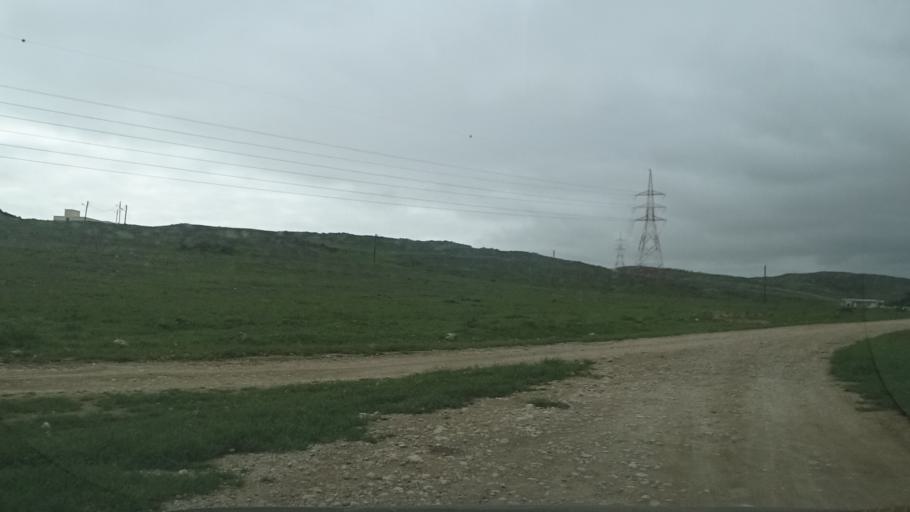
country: OM
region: Zufar
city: Salalah
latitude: 17.1114
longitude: 54.2369
